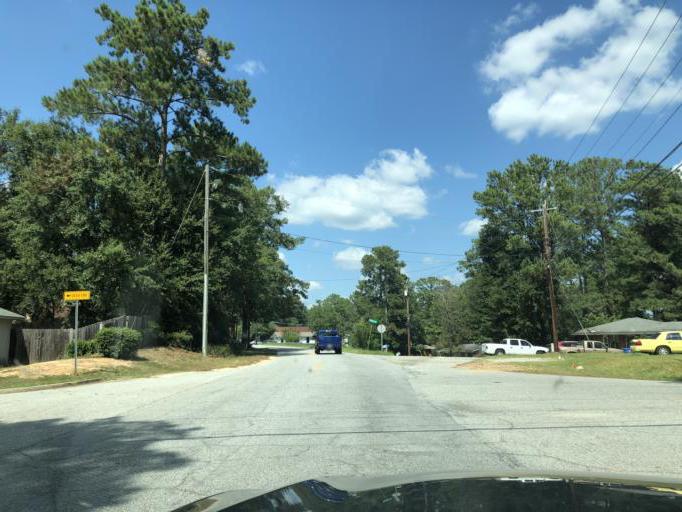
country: US
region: Georgia
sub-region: Muscogee County
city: Columbus
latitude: 32.4896
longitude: -84.9135
